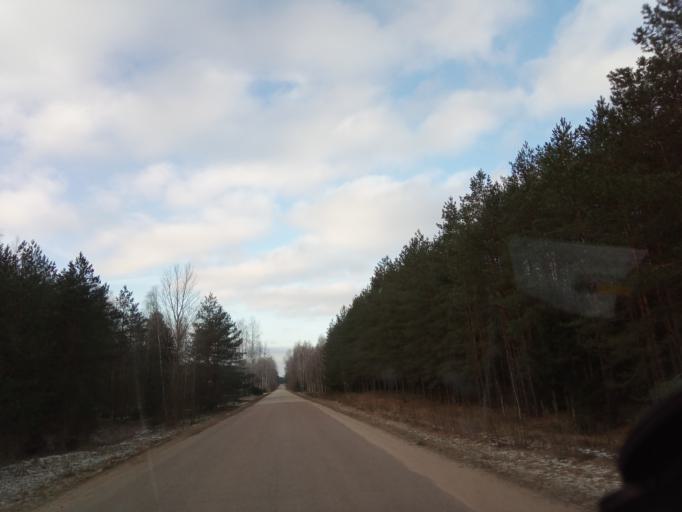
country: LT
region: Alytaus apskritis
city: Druskininkai
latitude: 53.9680
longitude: 24.2634
